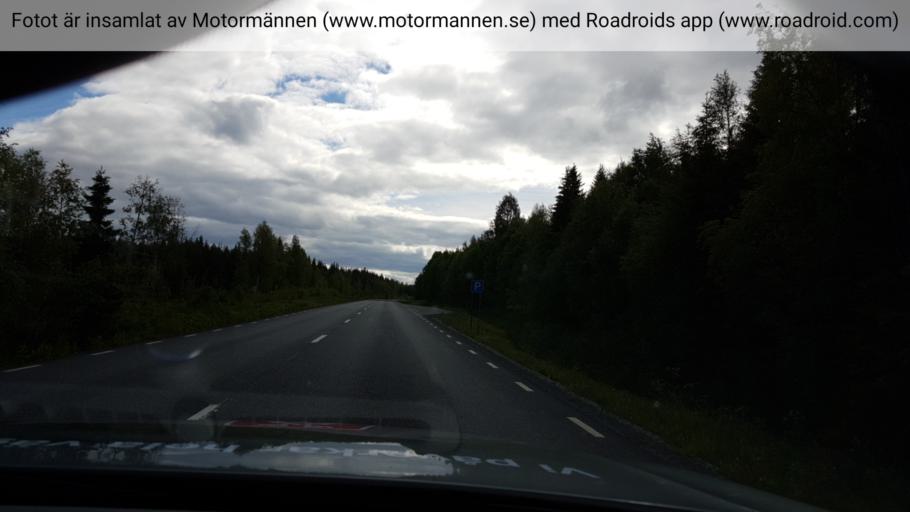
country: SE
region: Jaemtland
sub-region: Stroemsunds Kommun
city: Stroemsund
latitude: 64.1158
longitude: 15.6179
